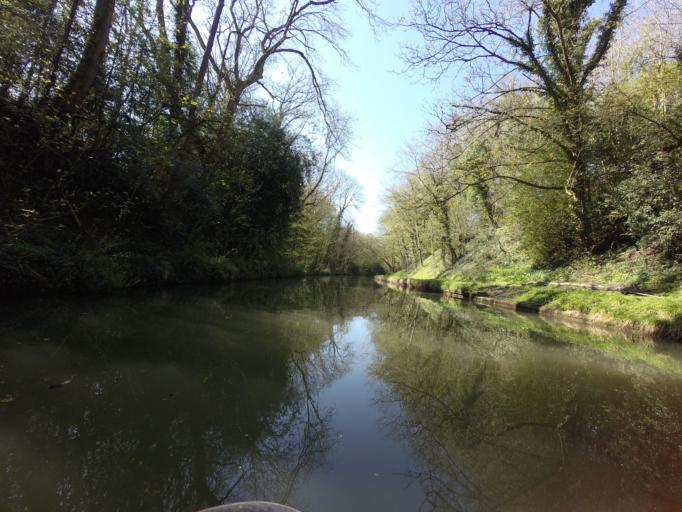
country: GB
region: England
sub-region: Hertfordshire
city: Tring
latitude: 51.8010
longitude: -0.6323
